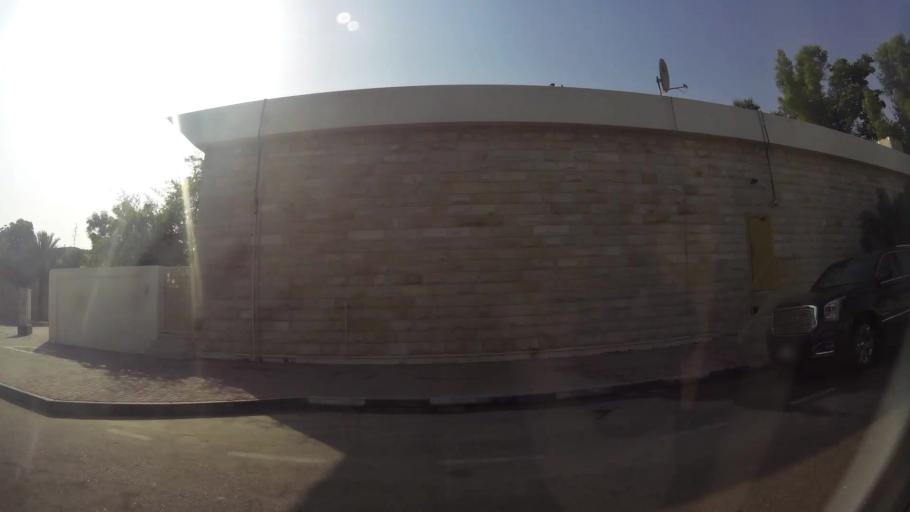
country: AE
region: Ash Shariqah
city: Sharjah
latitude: 25.3112
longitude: 55.3442
